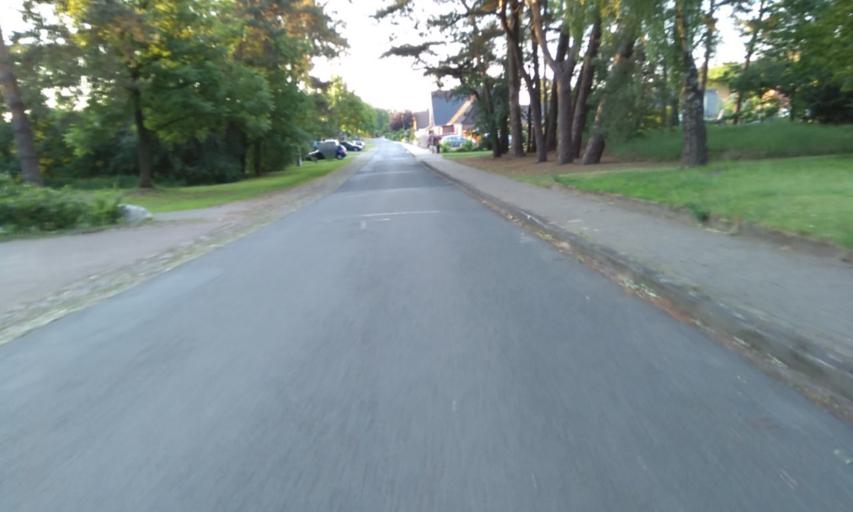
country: DE
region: Lower Saxony
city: Ahlerstedt
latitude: 53.4262
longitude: 9.4284
